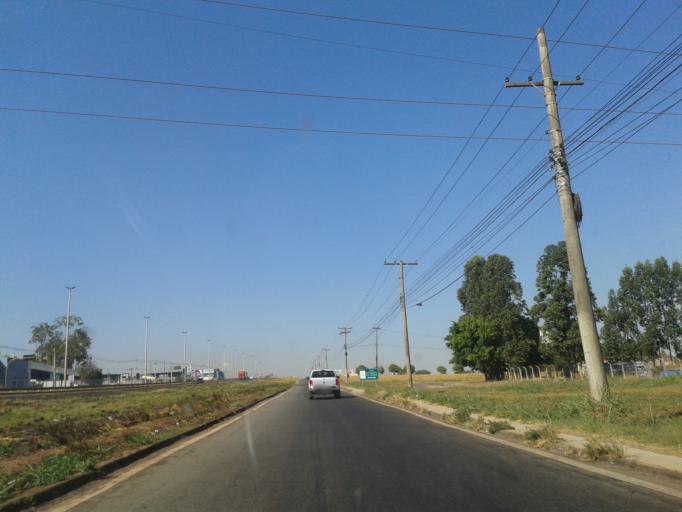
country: BR
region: Goias
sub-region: Aparecida De Goiania
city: Aparecida de Goiania
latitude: -16.7931
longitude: -49.2384
